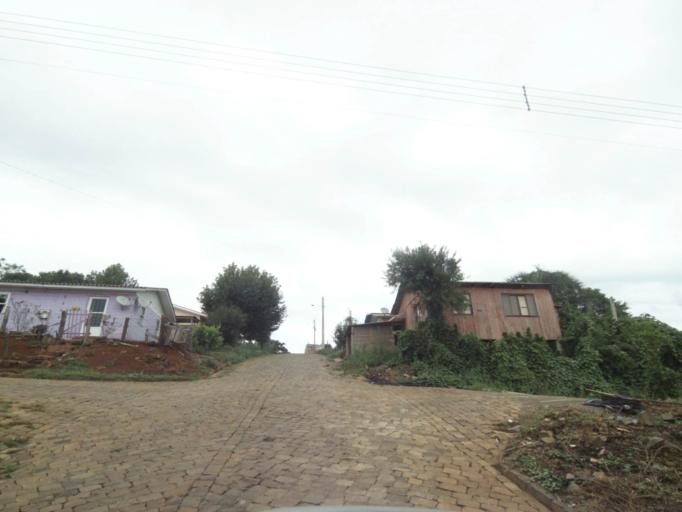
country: BR
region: Rio Grande do Sul
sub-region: Lagoa Vermelha
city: Lagoa Vermelha
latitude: -28.2168
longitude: -51.5389
